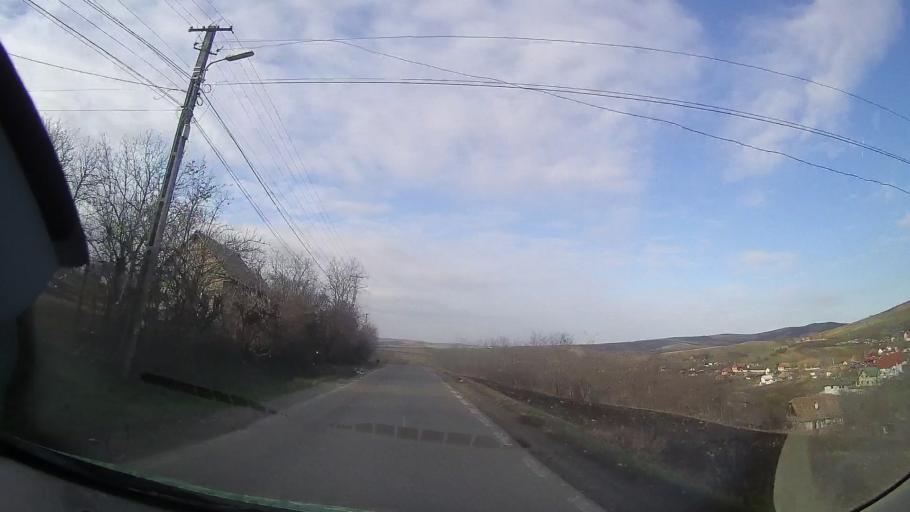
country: RO
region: Mures
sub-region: Comuna Sanger
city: Sanger
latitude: 46.5561
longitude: 24.1401
